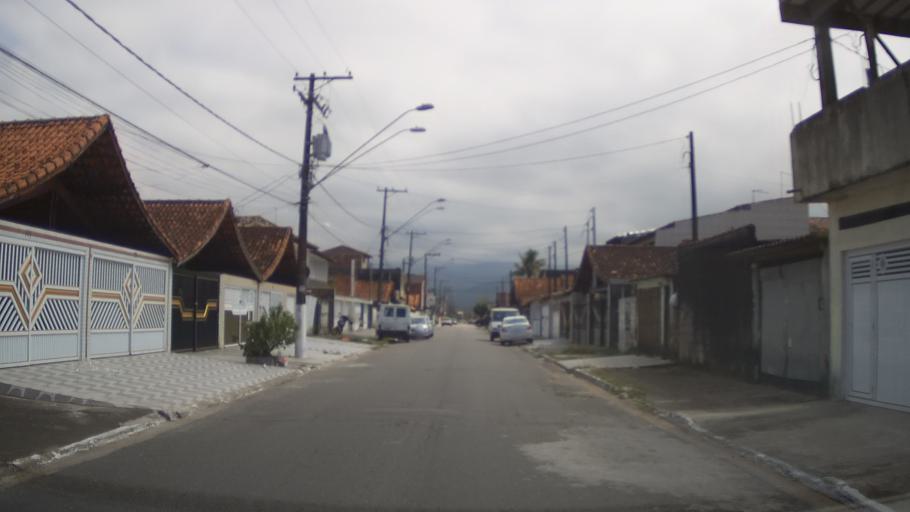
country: BR
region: Sao Paulo
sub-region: Praia Grande
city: Praia Grande
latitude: -24.0227
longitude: -46.4885
